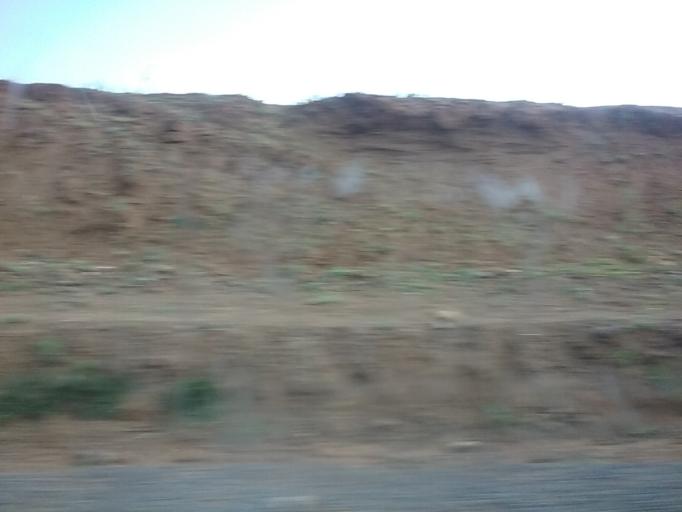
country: LS
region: Berea
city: Teyateyaneng
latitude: -29.0853
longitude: 27.9138
